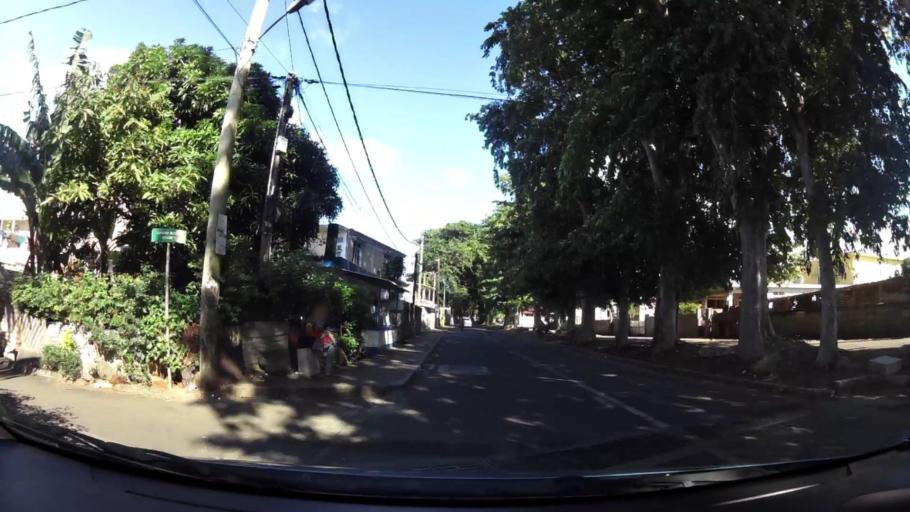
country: MU
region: Grand Port
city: Mahebourg
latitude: -20.4074
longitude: 57.6996
